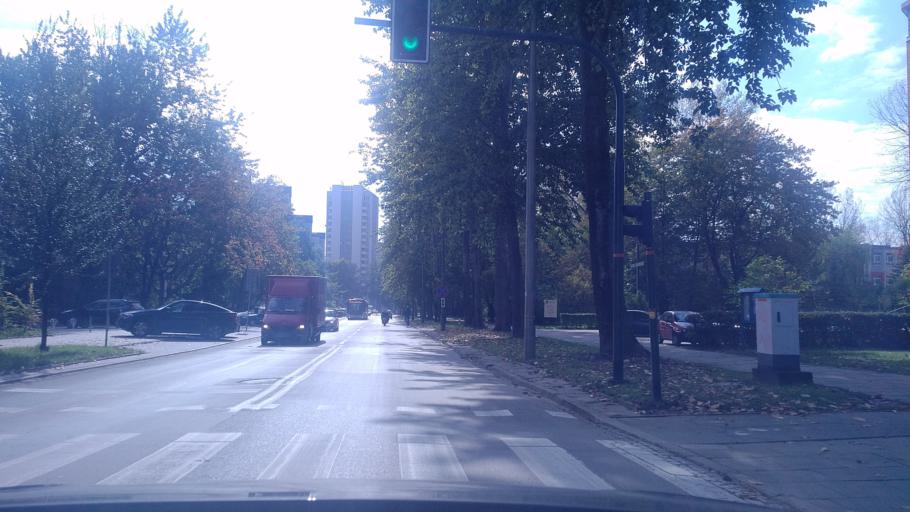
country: PL
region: Lesser Poland Voivodeship
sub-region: Krakow
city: Krakow
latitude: 50.0771
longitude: 19.9175
